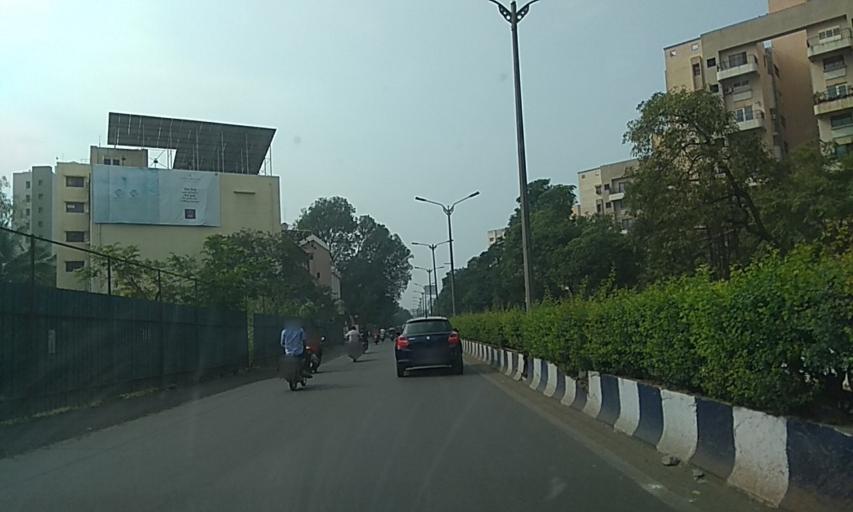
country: IN
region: Maharashtra
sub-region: Pune Division
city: Pune
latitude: 18.5109
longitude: 73.9321
